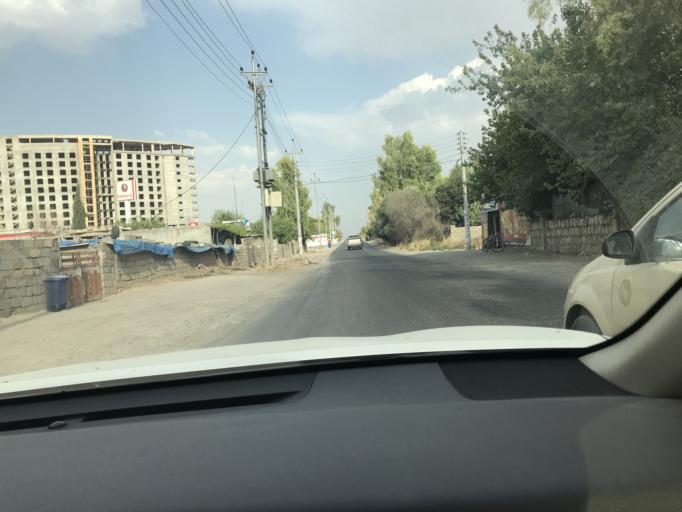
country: IQ
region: Arbil
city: Erbil
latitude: 36.2082
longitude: 43.9562
